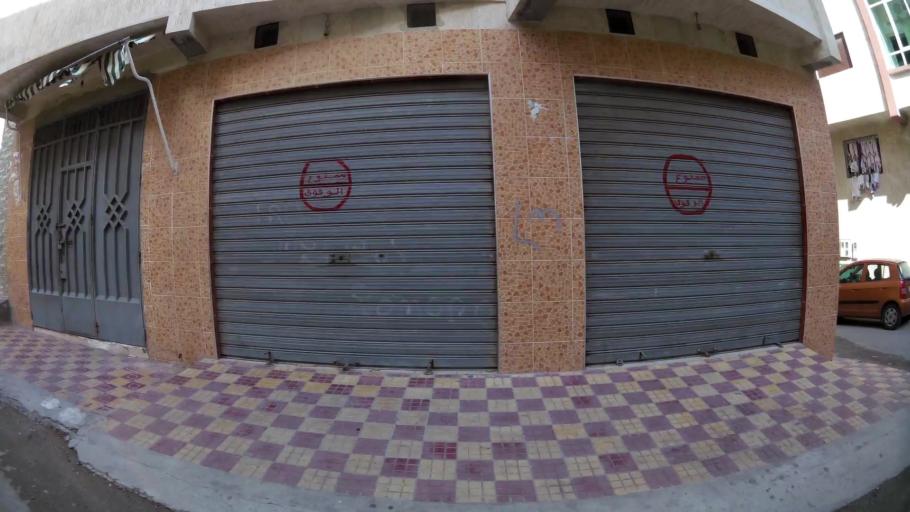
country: MA
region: Tanger-Tetouan
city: Tetouan
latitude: 35.5896
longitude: -5.3504
